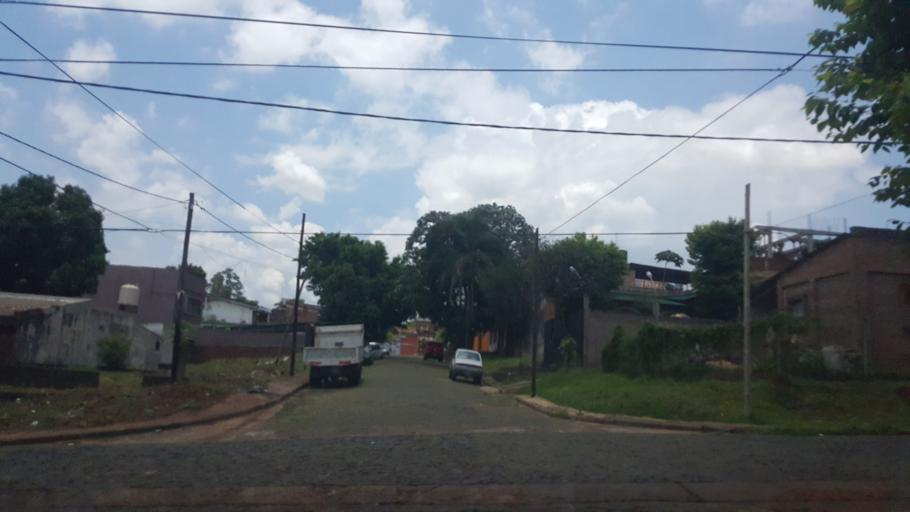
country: AR
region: Misiones
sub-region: Departamento de Capital
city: Posadas
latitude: -27.3844
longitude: -55.9069
